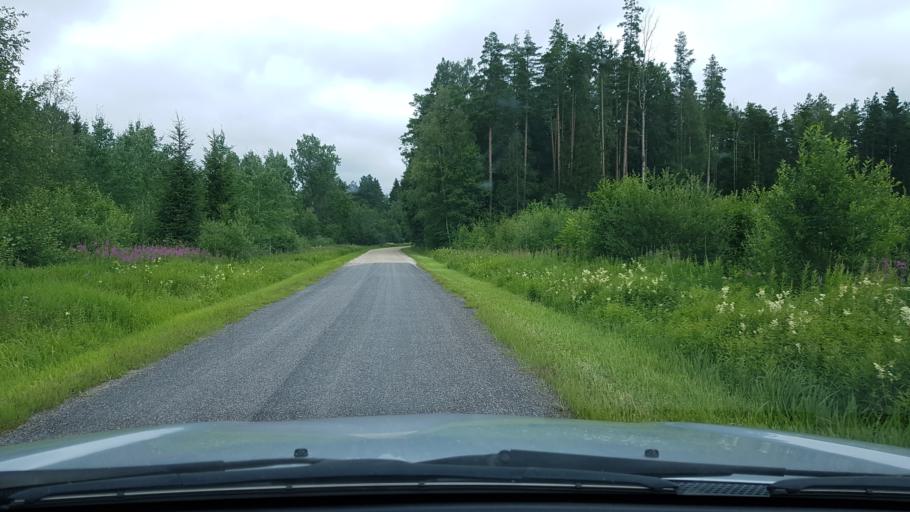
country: EE
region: Ida-Virumaa
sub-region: Narva-Joesuu linn
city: Narva-Joesuu
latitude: 59.3574
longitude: 28.0404
